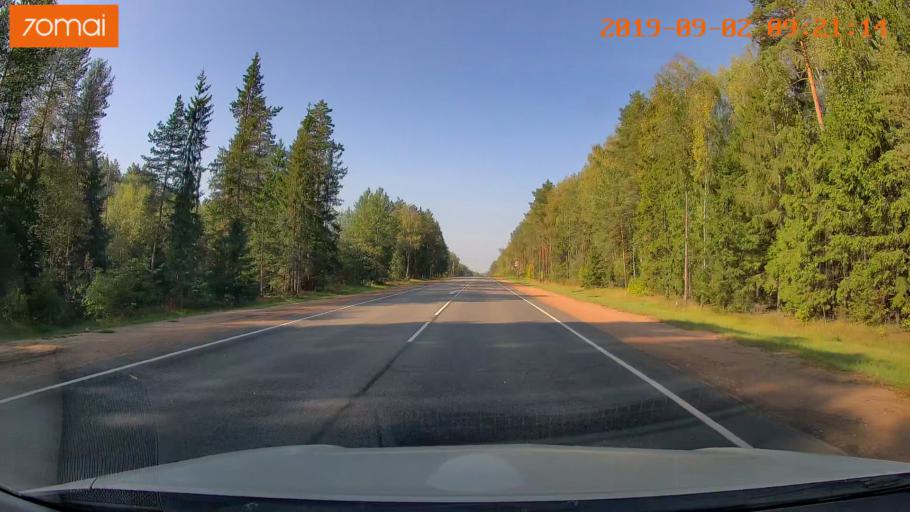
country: RU
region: Kaluga
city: Yukhnov
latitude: 54.7936
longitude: 35.3643
